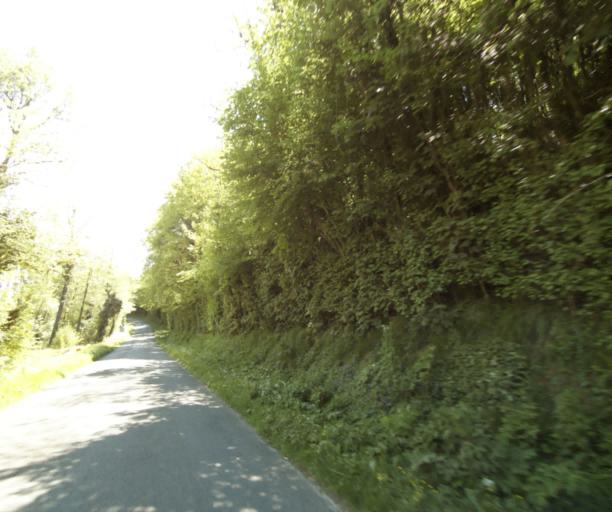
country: FR
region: Poitou-Charentes
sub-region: Departement de la Charente-Maritime
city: Chaniers
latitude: 45.7486
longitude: -0.5095
